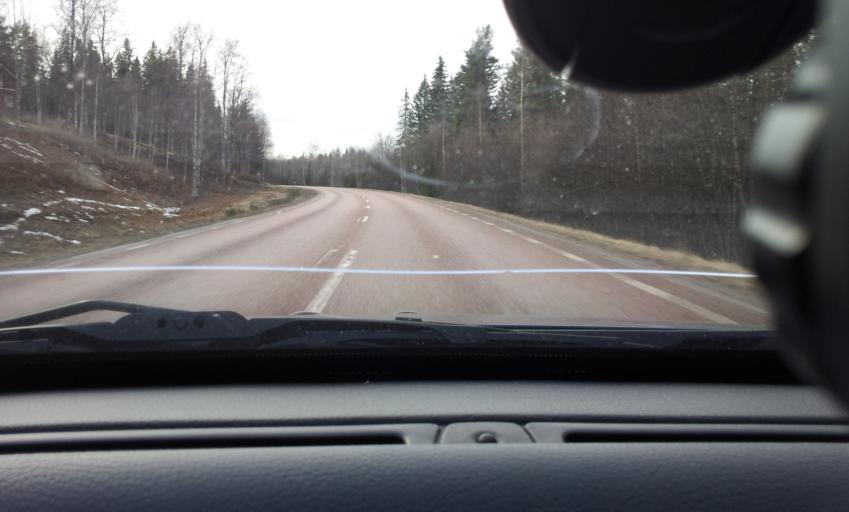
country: SE
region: Gaevleborg
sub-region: Ljusdals Kommun
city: Farila
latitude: 61.8841
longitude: 15.7060
